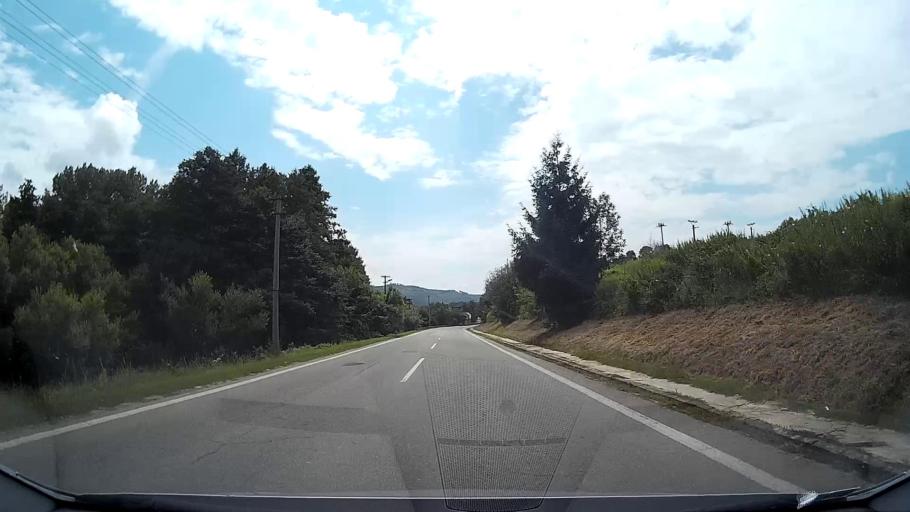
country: SK
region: Banskobystricky
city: Tisovec
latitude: 48.5631
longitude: 19.9574
